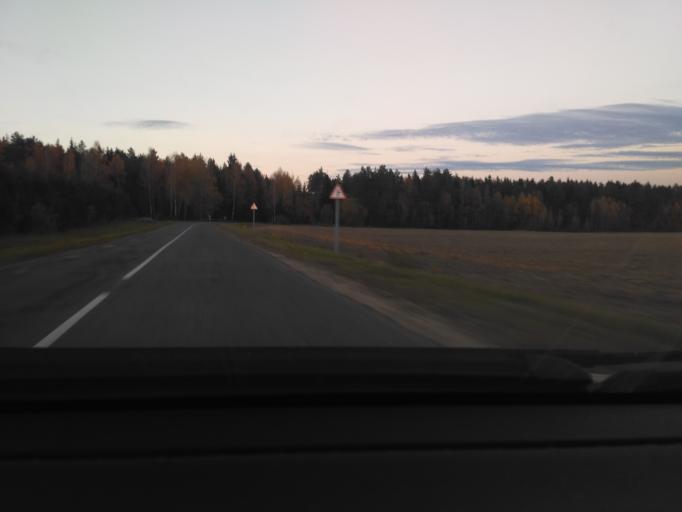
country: BY
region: Minsk
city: Loshnitsa
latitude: 54.3692
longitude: 28.6233
